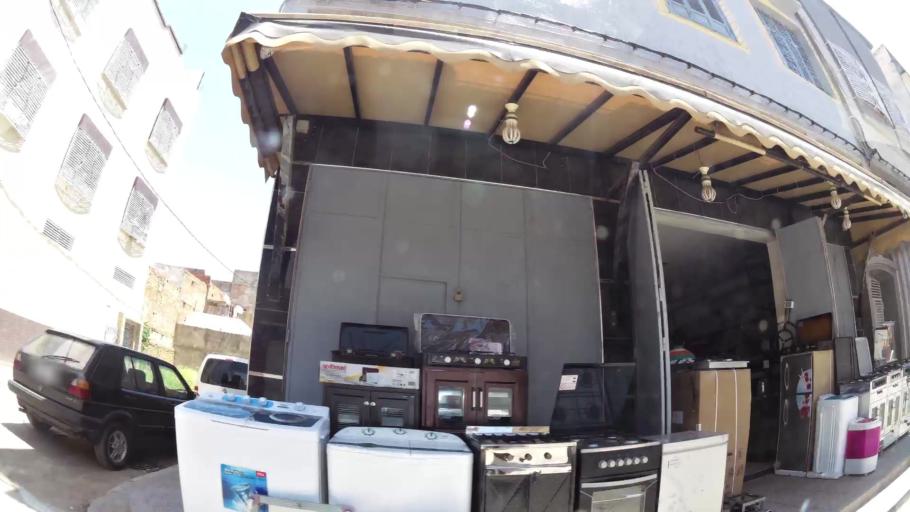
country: MA
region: Rabat-Sale-Zemmour-Zaer
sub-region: Khemisset
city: Khemisset
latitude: 33.8283
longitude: -6.0737
